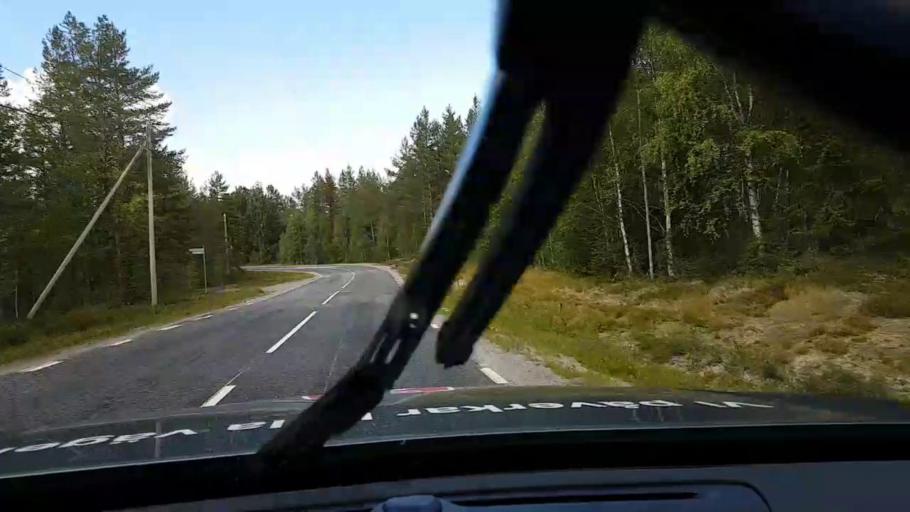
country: SE
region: Vaesterbotten
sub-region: Asele Kommun
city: Asele
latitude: 63.7901
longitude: 17.5848
